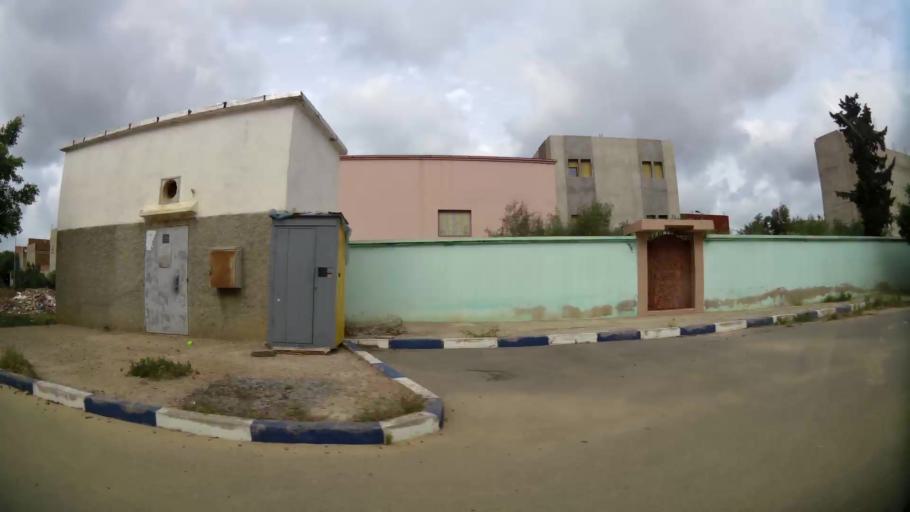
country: MA
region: Oriental
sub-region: Nador
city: Nador
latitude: 35.1587
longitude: -2.9184
